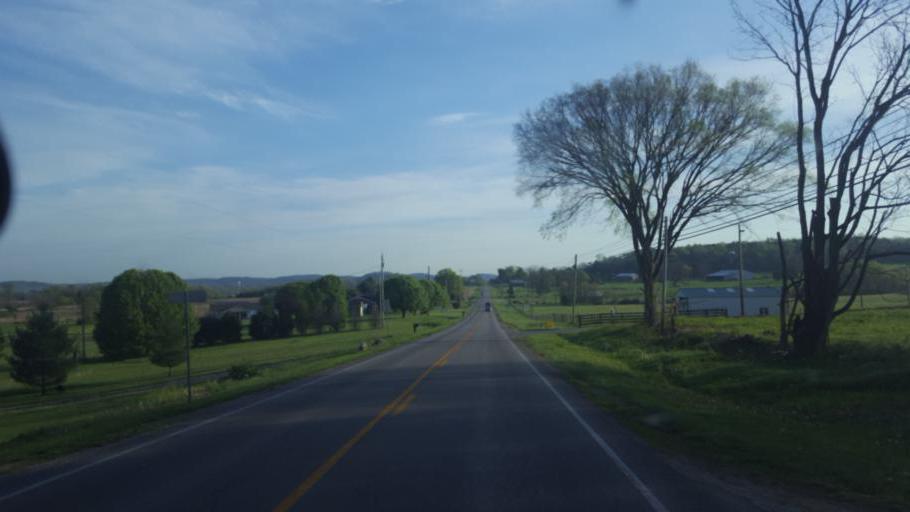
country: US
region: Kentucky
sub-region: Hart County
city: Munfordville
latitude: 37.2435
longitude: -85.8921
